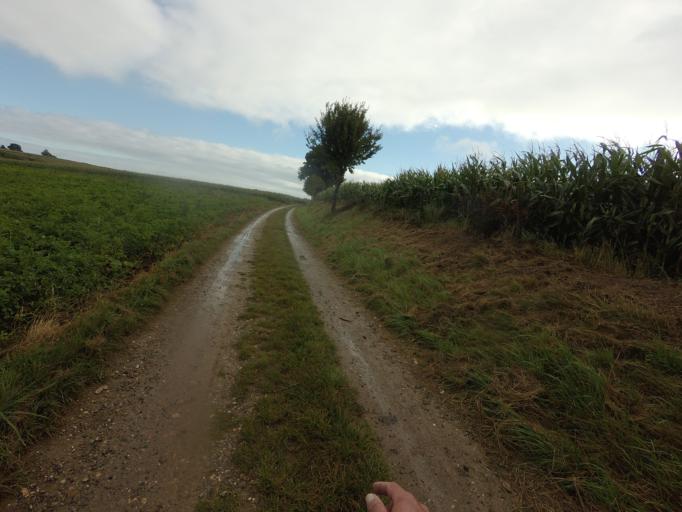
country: BE
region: Flanders
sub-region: Provincie Limburg
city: Sint-Pieters-Voeren
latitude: 50.7794
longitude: 5.8139
